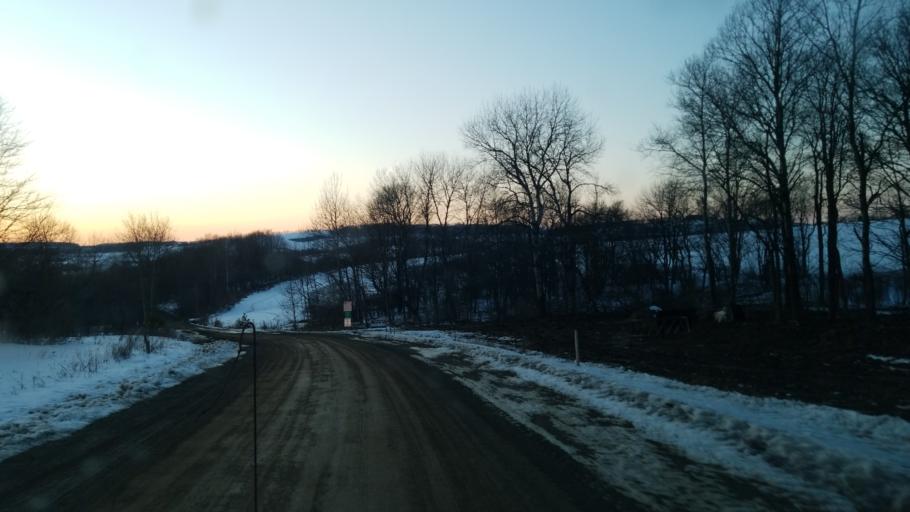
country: US
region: New York
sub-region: Allegany County
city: Andover
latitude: 42.0080
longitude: -77.7489
